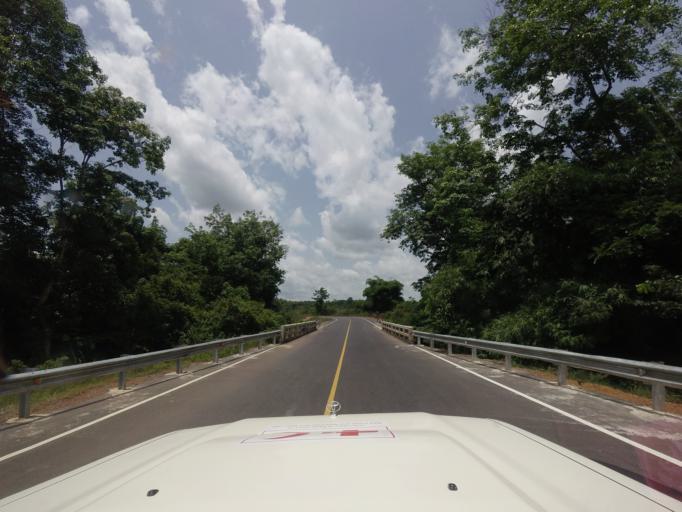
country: LR
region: Margibi
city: Kakata
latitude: 6.4916
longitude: -10.3941
